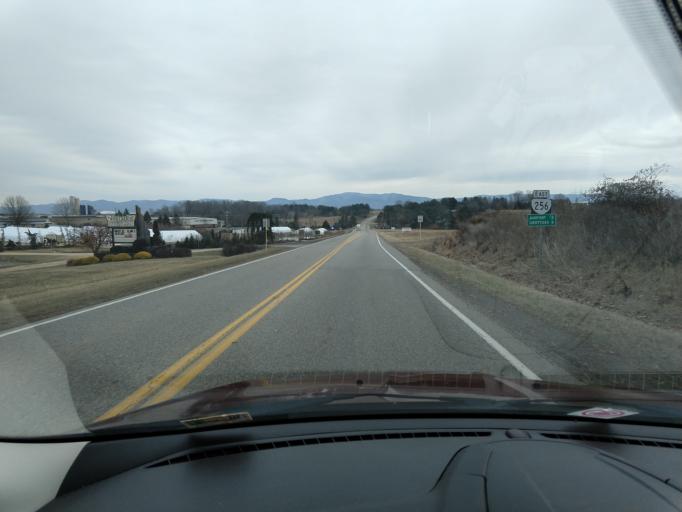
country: US
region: Virginia
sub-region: Augusta County
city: Weyers Cave
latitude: 38.2841
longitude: -78.9103
